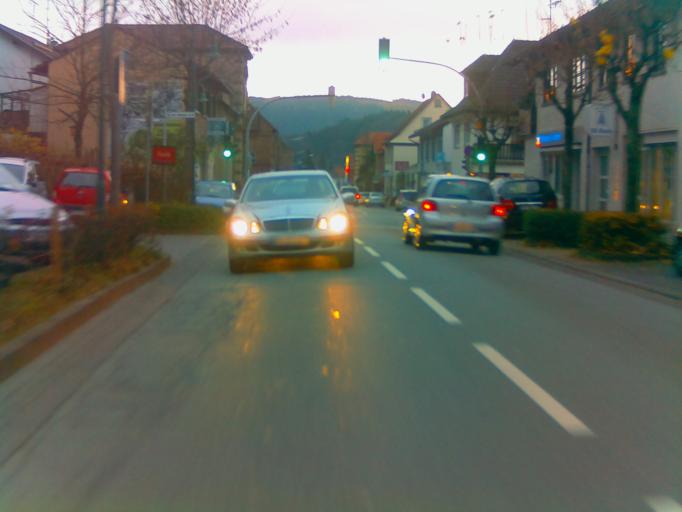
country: DE
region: Hesse
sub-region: Regierungsbezirk Darmstadt
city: Wald-Michelbach
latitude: 49.5717
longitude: 8.8256
